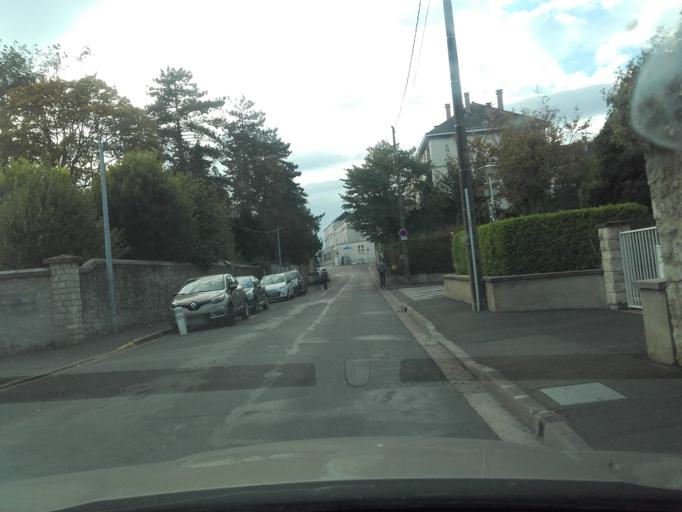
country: FR
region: Centre
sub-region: Departement d'Indre-et-Loire
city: Tours
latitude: 47.4066
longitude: 0.6905
